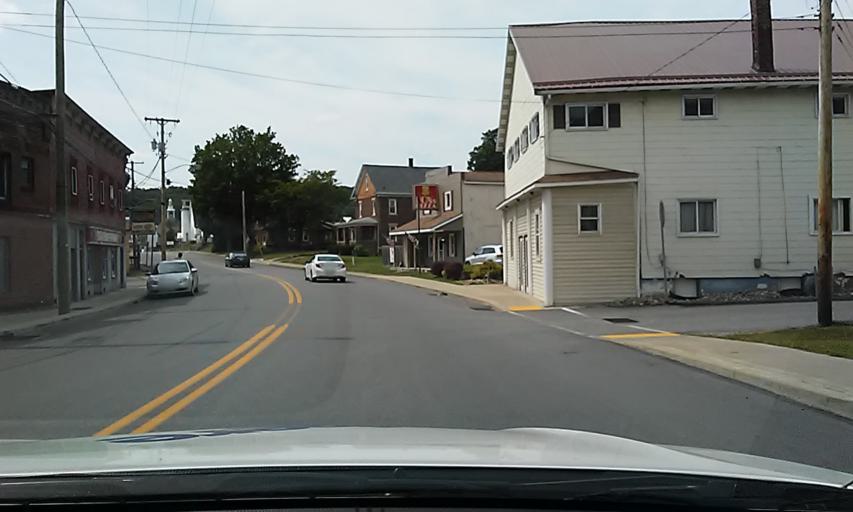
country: US
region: Pennsylvania
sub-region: Jefferson County
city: Sykesville
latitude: 41.0520
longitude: -78.8178
